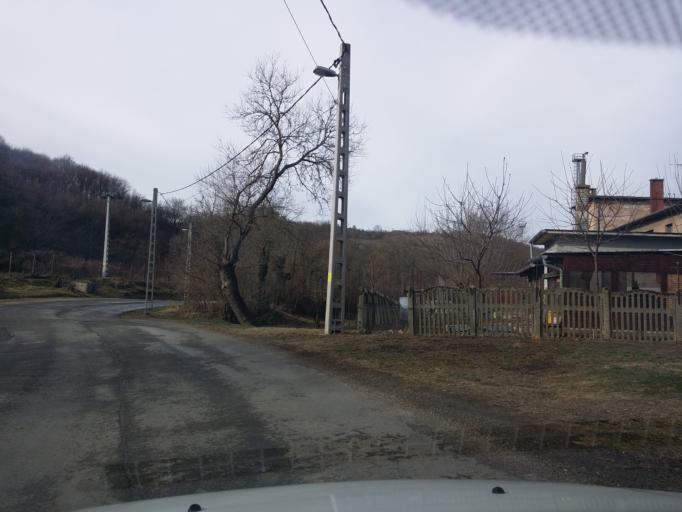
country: HU
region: Baranya
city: Villany
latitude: 45.8768
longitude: 18.4501
